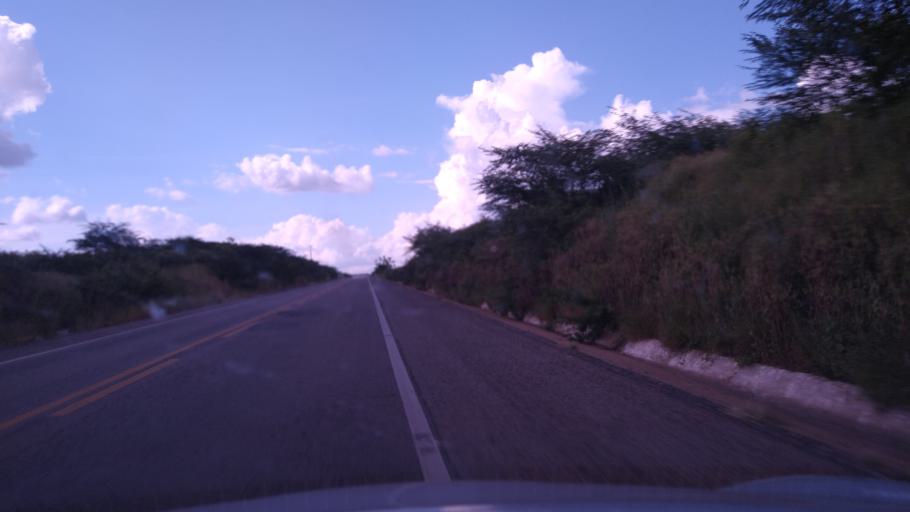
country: BR
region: Ceara
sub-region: Caninde
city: Caninde
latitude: -4.3925
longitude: -39.3139
